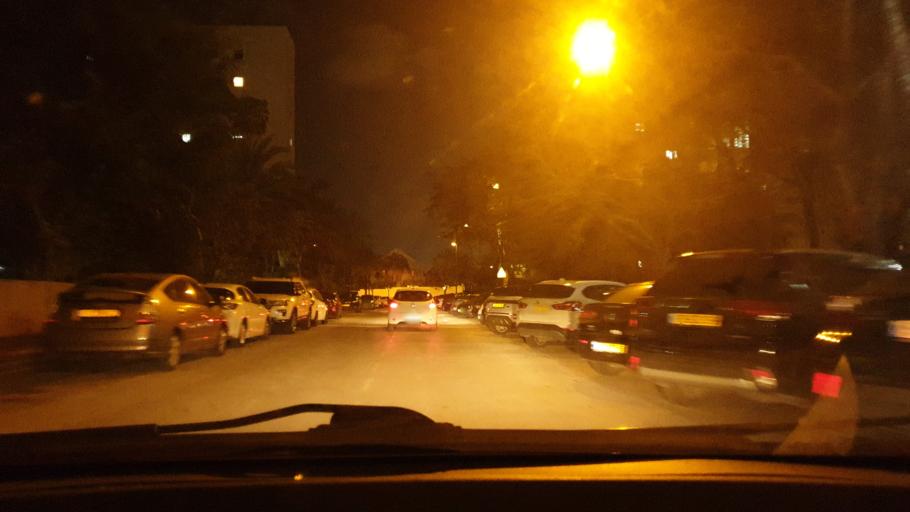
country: IL
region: Tel Aviv
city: Ramat HaSharon
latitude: 32.1266
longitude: 34.8012
